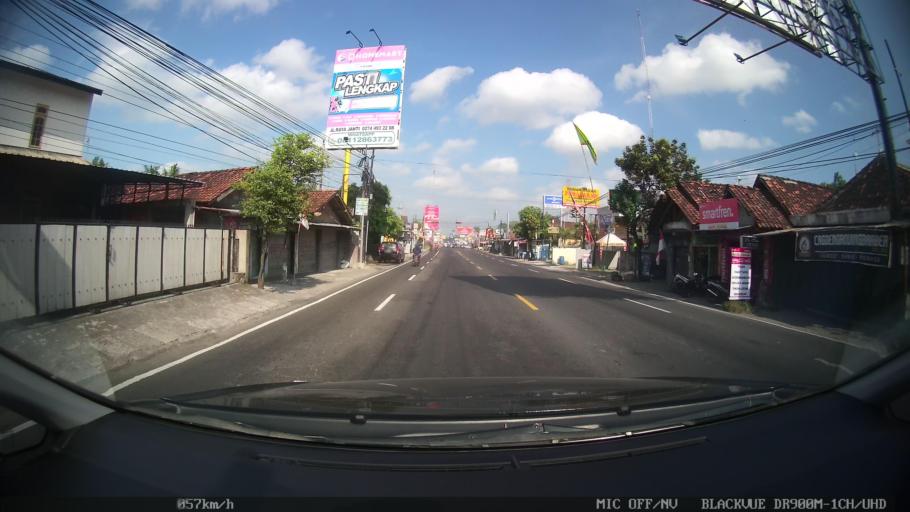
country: ID
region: Daerah Istimewa Yogyakarta
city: Godean
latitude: -7.8120
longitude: 110.2724
